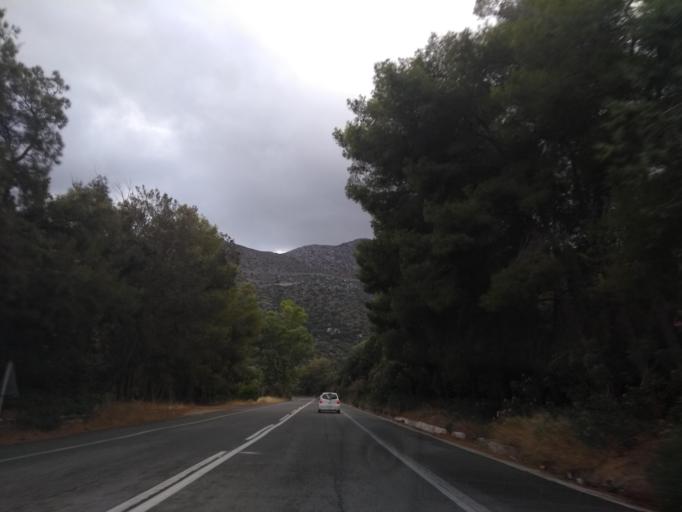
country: GR
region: Crete
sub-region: Nomos Rethymnis
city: Anogeia
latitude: 35.3897
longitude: 24.8819
